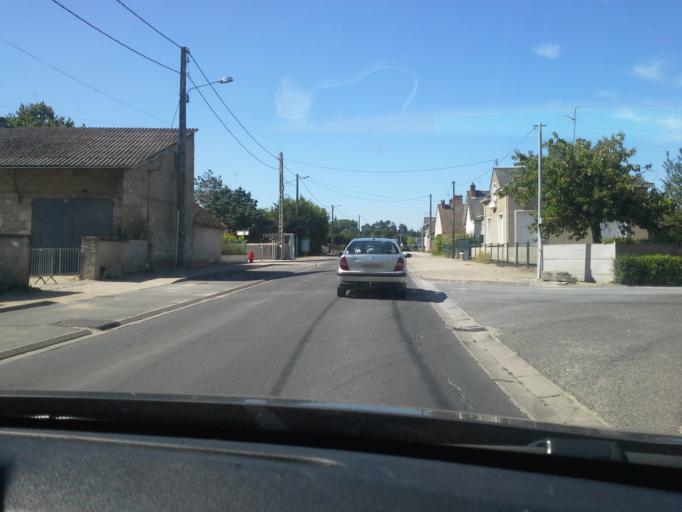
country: FR
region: Centre
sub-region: Departement du Loir-et-Cher
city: Cormeray
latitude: 47.4923
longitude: 1.4061
